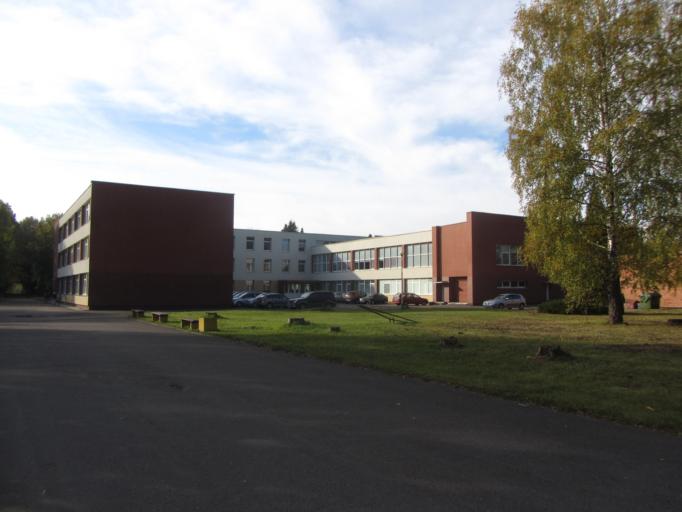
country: LT
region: Vilnius County
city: Elektrenai
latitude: 54.7819
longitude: 24.6558
